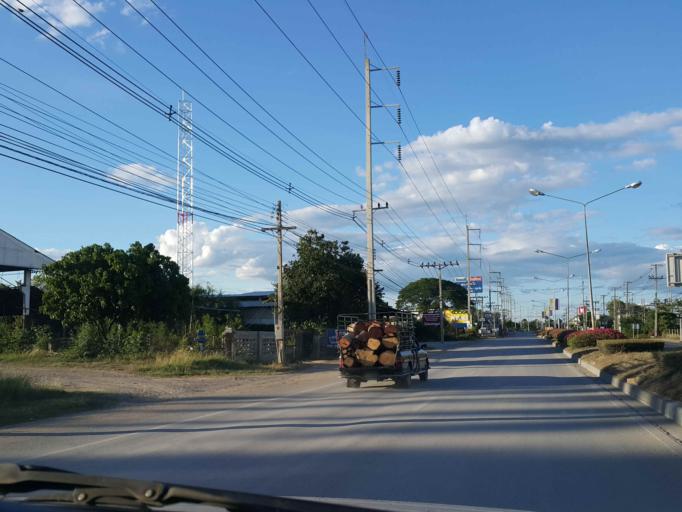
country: TH
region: Chiang Mai
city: Chom Thong
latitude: 18.4367
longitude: 98.6874
